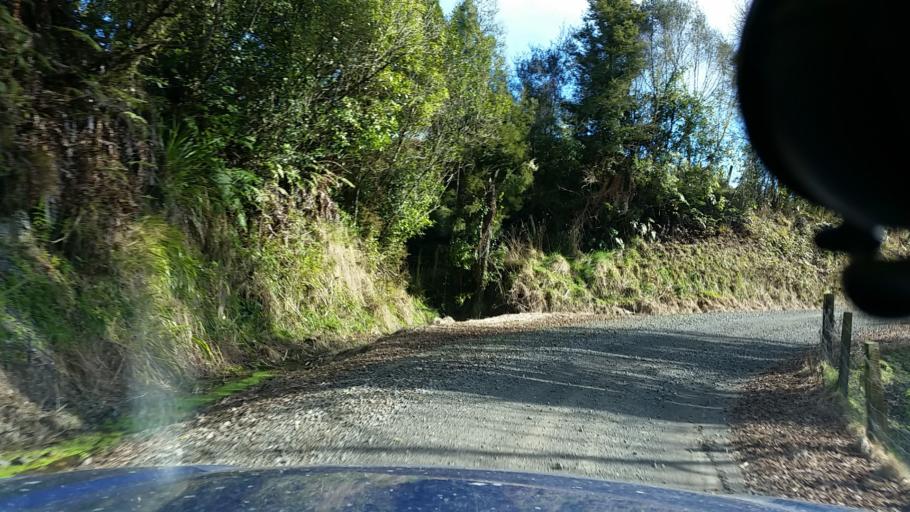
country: NZ
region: Taranaki
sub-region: New Plymouth District
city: Waitara
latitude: -39.0346
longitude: 174.7793
